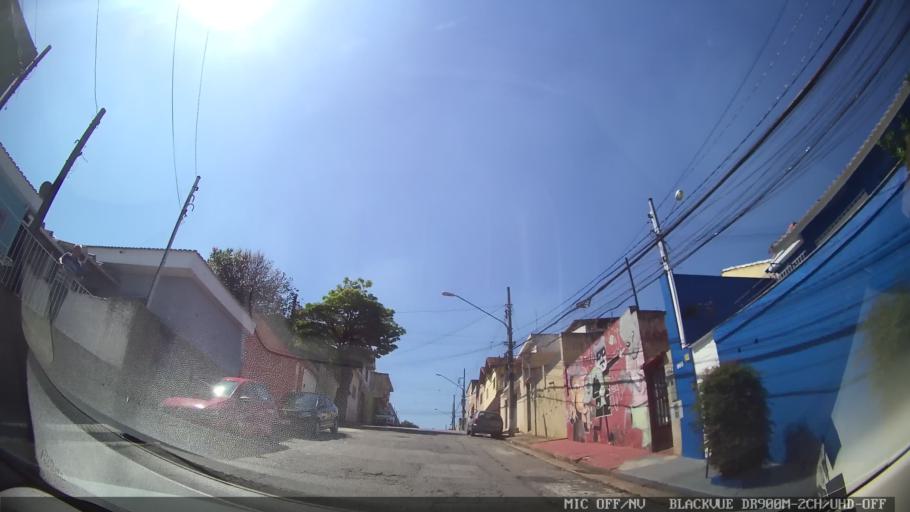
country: BR
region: Sao Paulo
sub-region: Sao Paulo
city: Sao Paulo
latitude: -23.4954
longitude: -46.6551
